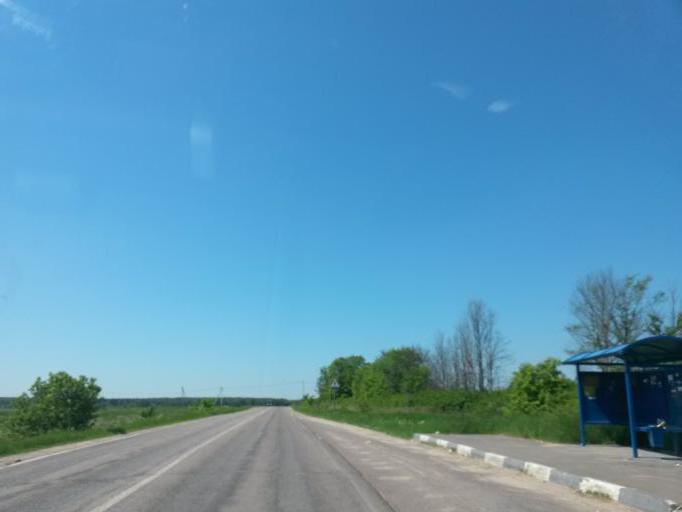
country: RU
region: Moskovskaya
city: Lyubuchany
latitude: 55.2509
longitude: 37.6060
